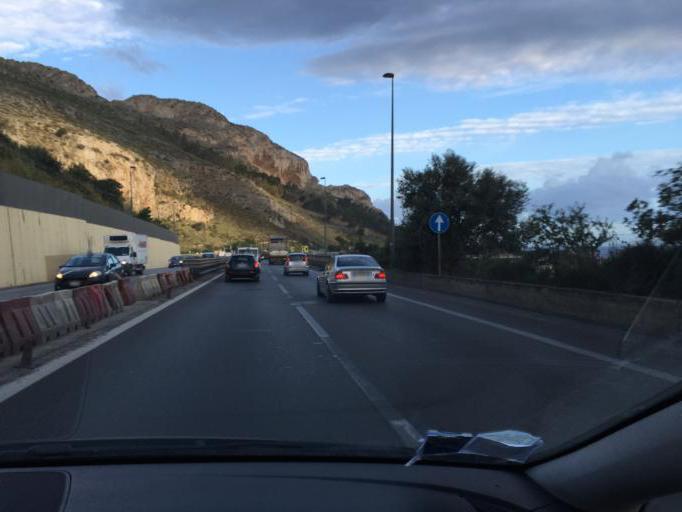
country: IT
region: Sicily
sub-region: Palermo
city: Isola delle Femmine
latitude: 38.1949
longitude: 13.2767
